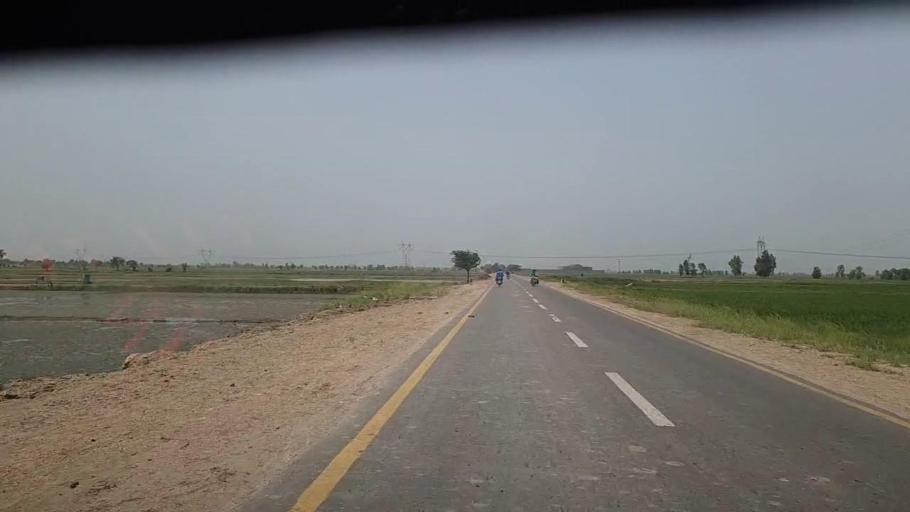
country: PK
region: Sindh
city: Sita Road
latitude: 27.0406
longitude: 67.8764
